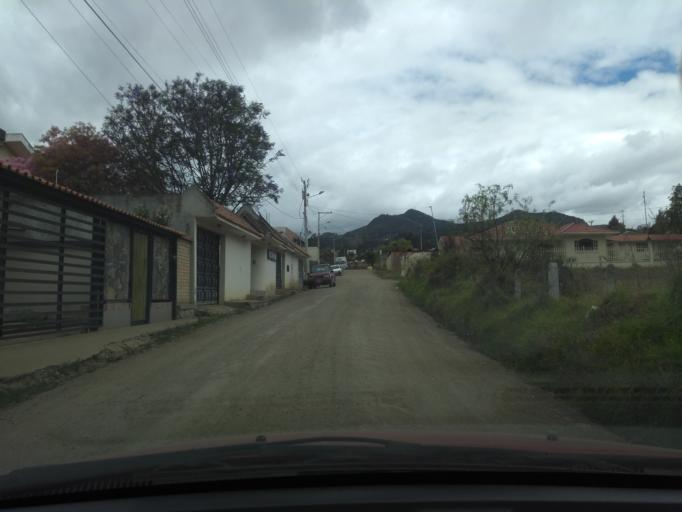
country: EC
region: Azuay
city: Llacao
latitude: -2.8533
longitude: -78.9172
